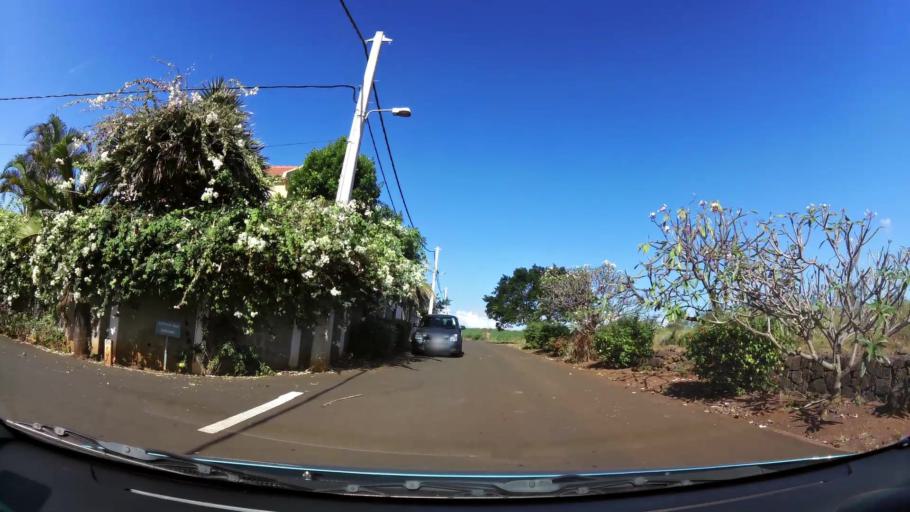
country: MU
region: Black River
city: Albion
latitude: -20.2204
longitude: 57.4034
